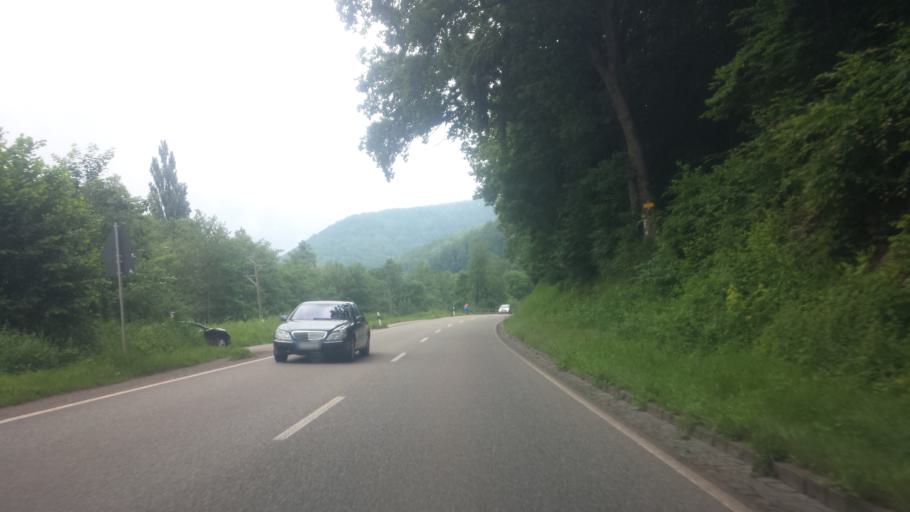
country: DE
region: Rheinland-Pfalz
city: Eschbach
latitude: 49.1589
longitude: 8.0071
